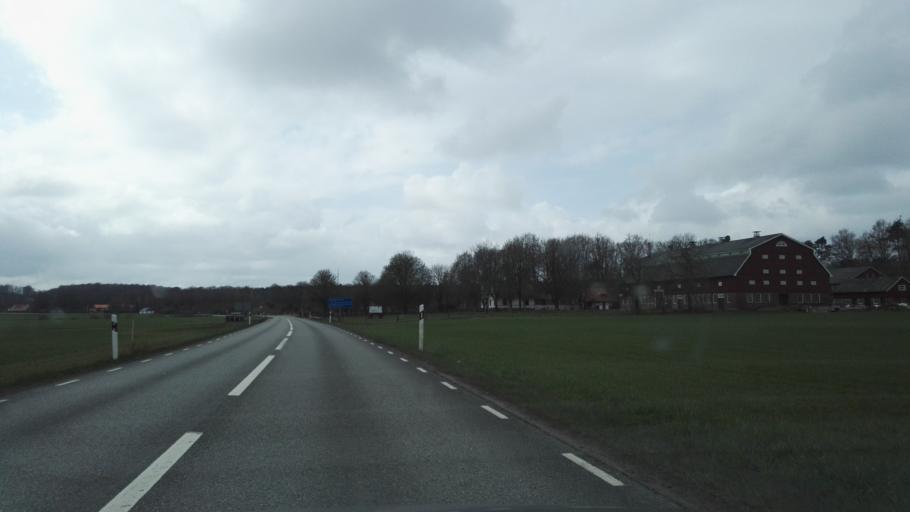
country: SE
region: Skane
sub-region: Hassleholms Kommun
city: Hassleholm
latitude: 56.1824
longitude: 13.8539
